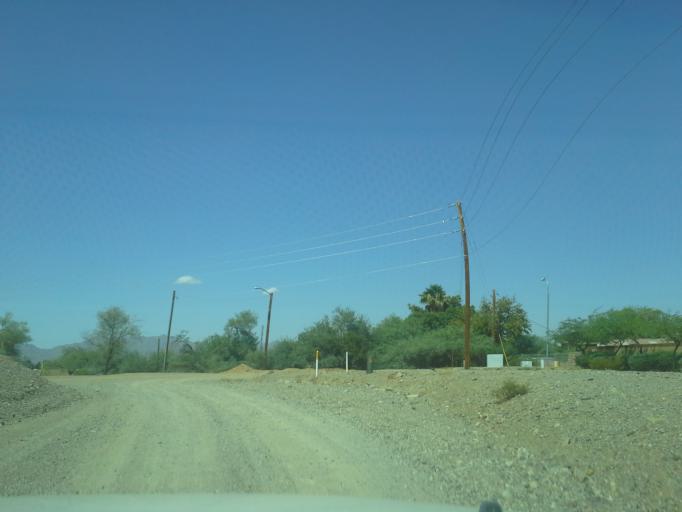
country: US
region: Arizona
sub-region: Maricopa County
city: Laveen
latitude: 33.3520
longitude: -112.1598
